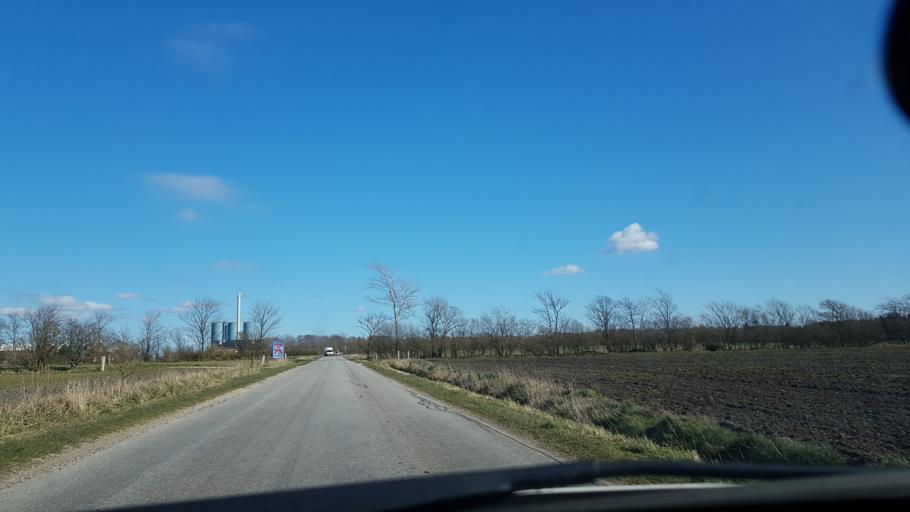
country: DK
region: South Denmark
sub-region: Tonder Kommune
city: Sherrebek
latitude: 55.2219
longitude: 8.8287
